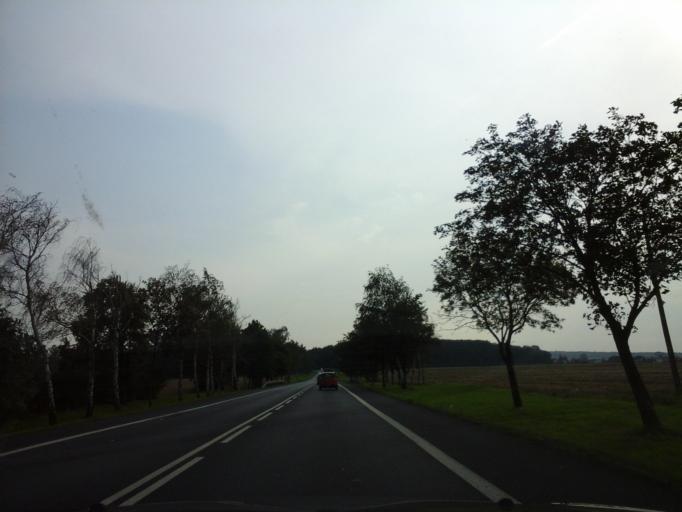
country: PL
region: Greater Poland Voivodeship
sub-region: Powiat koscianski
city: Smigiel
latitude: 52.0410
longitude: 16.5506
